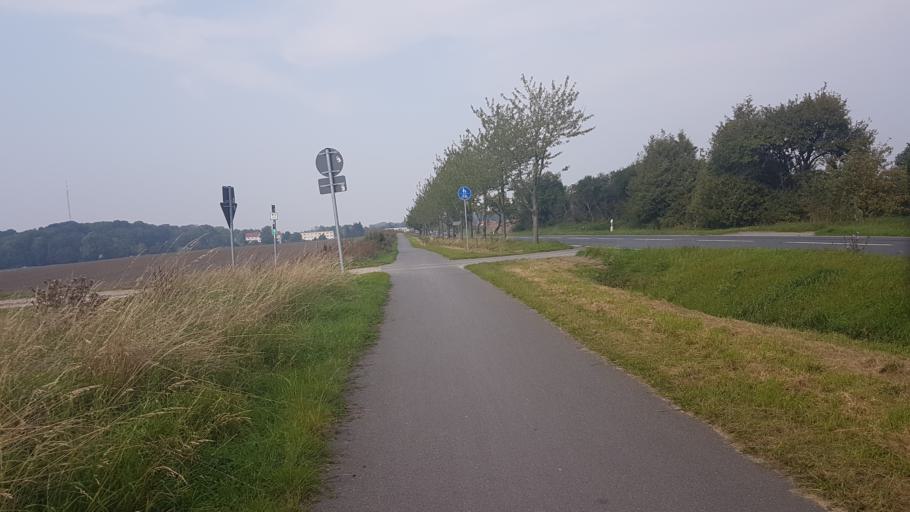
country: DE
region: Mecklenburg-Vorpommern
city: Garz
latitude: 54.3071
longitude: 13.3516
